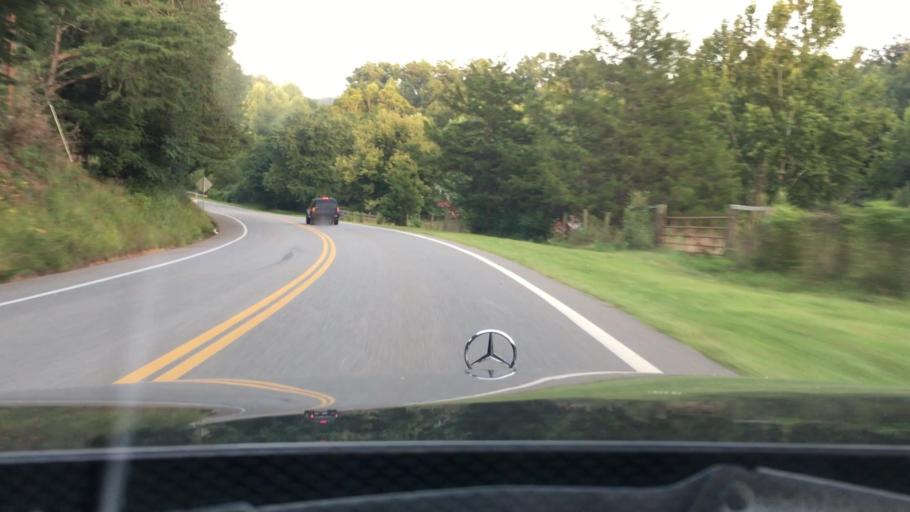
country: US
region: Virginia
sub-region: Campbell County
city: Altavista
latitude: 37.1296
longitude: -79.2792
